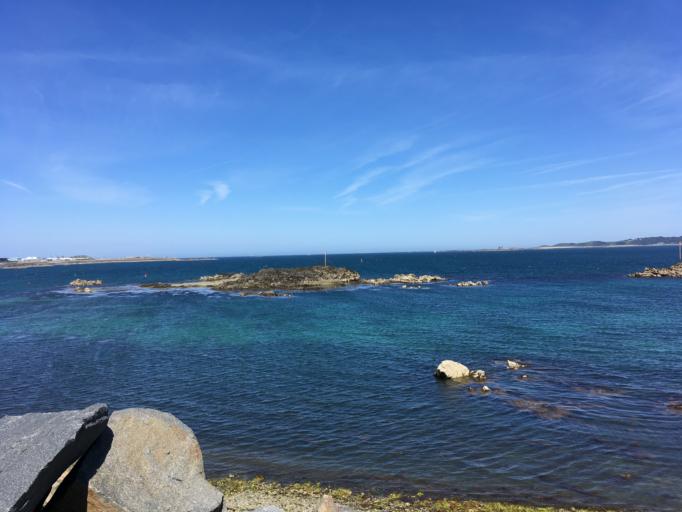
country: GG
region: St Peter Port
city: Saint Peter Port
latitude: 49.4590
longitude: -2.5284
